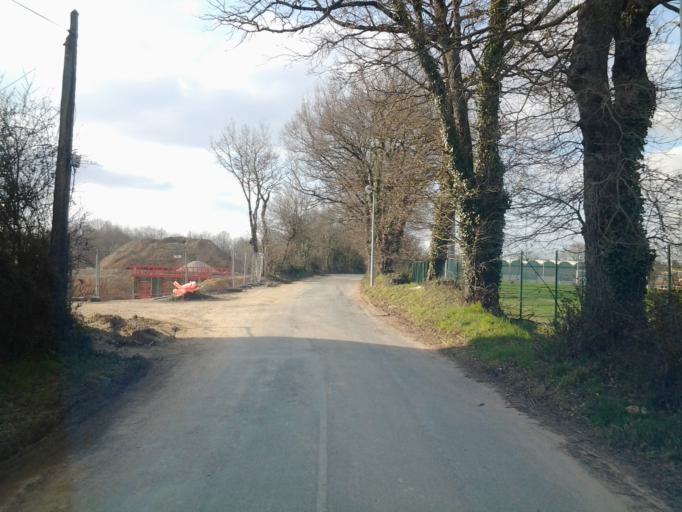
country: FR
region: Pays de la Loire
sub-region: Departement de la Vendee
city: La Roche-sur-Yon
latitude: 46.6577
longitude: -1.4059
